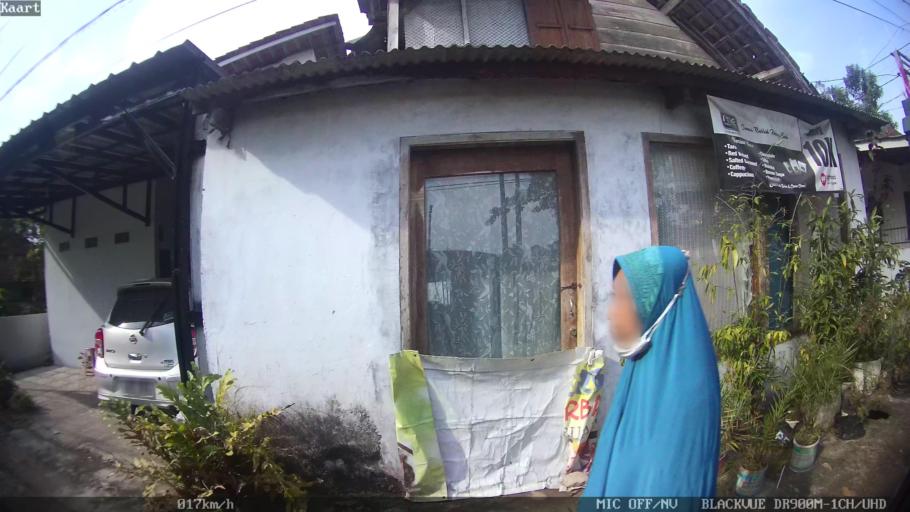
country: ID
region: Lampung
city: Bandarlampung
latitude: -5.4056
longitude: 105.2635
